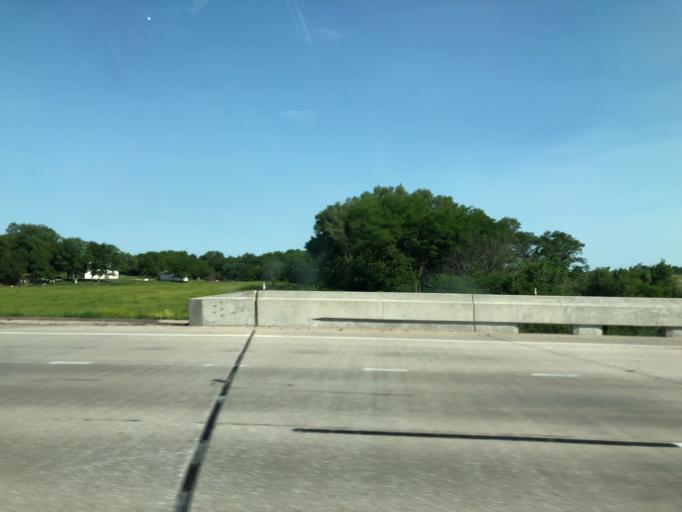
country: US
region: Nebraska
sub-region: Lancaster County
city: Waverly
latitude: 40.9278
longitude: -96.4494
